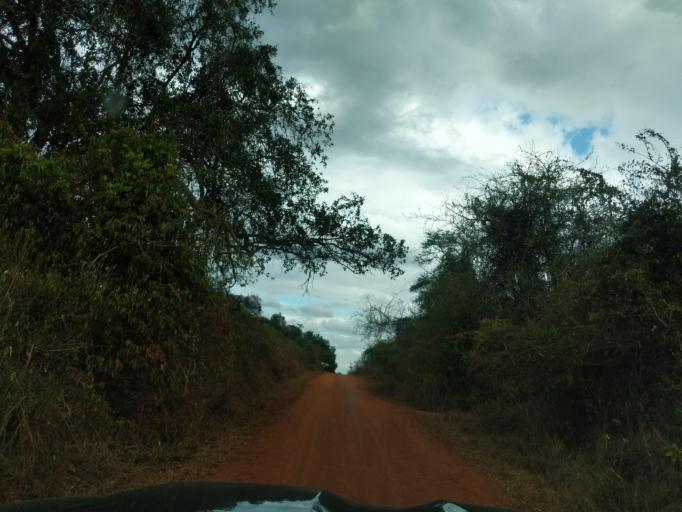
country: TZ
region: Pwani
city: Mvomero
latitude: -5.9314
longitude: 38.4197
